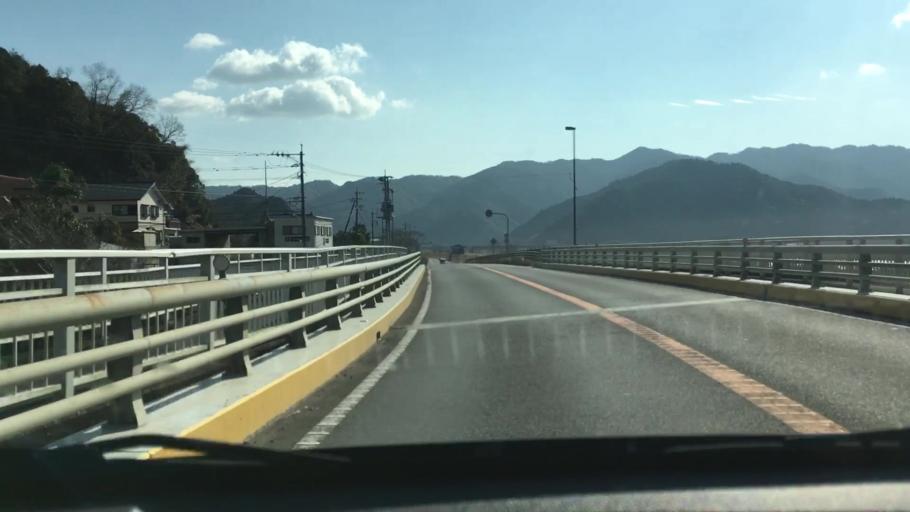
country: JP
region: Oita
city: Saiki
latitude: 32.9625
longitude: 131.8385
